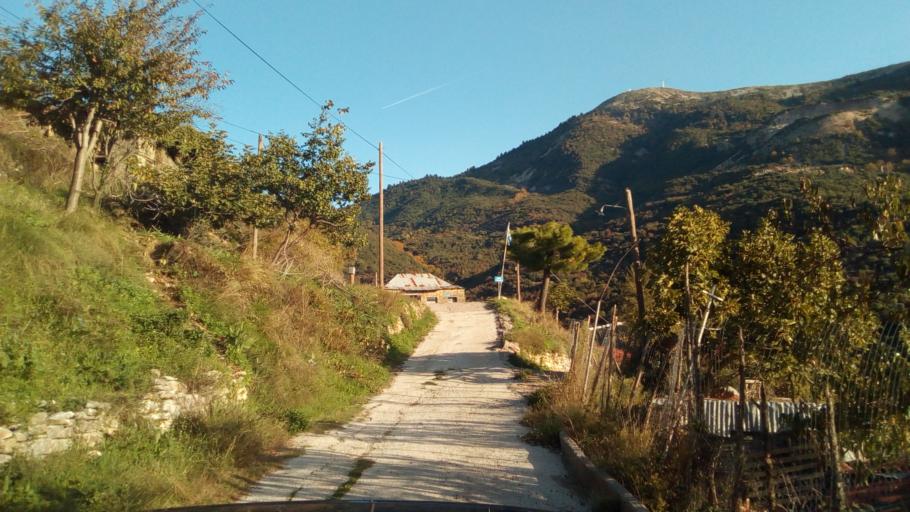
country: GR
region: West Greece
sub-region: Nomos Aitolias kai Akarnanias
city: Thermo
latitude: 38.5947
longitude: 21.7995
